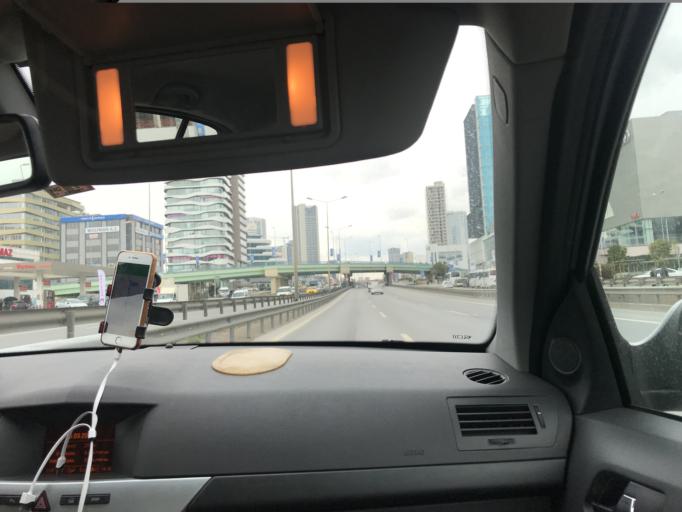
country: TR
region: Istanbul
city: Pendik
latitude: 40.8942
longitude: 29.2292
